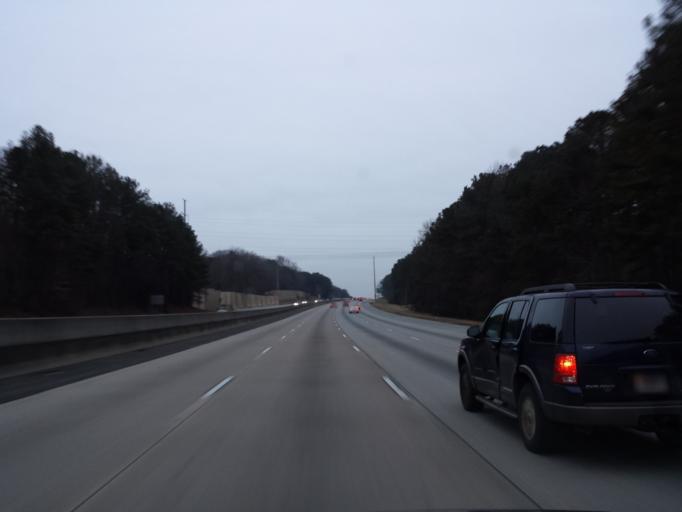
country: US
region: Georgia
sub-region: DeKalb County
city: Dunwoody
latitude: 33.9680
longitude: -84.3490
